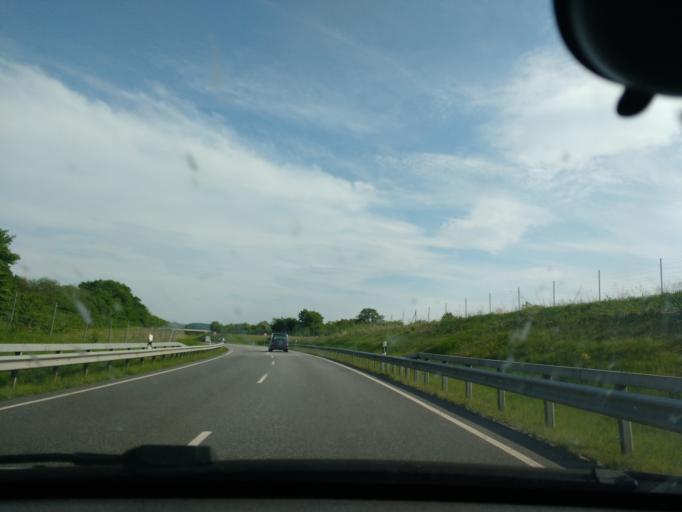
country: DE
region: Schleswig-Holstein
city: Gross Sarau
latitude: 53.7639
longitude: 10.7198
